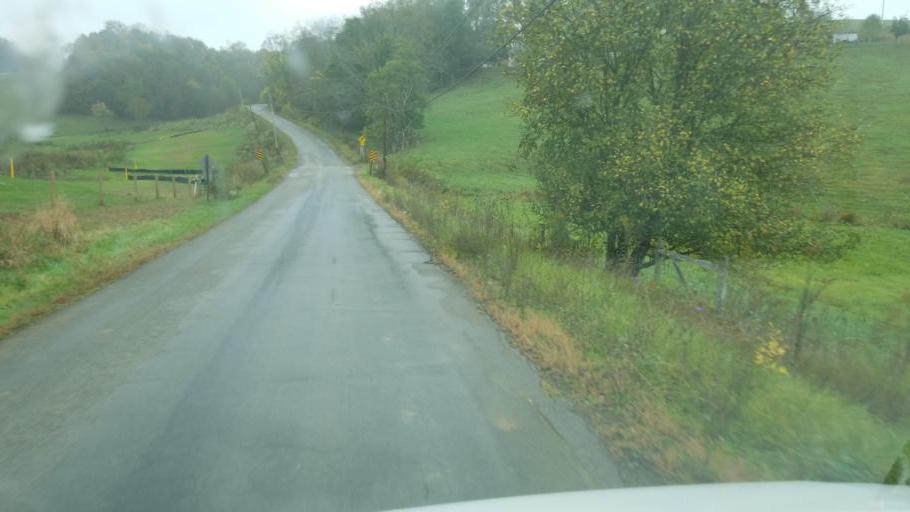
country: US
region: Ohio
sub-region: Harrison County
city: Cadiz
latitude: 40.3774
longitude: -81.0733
